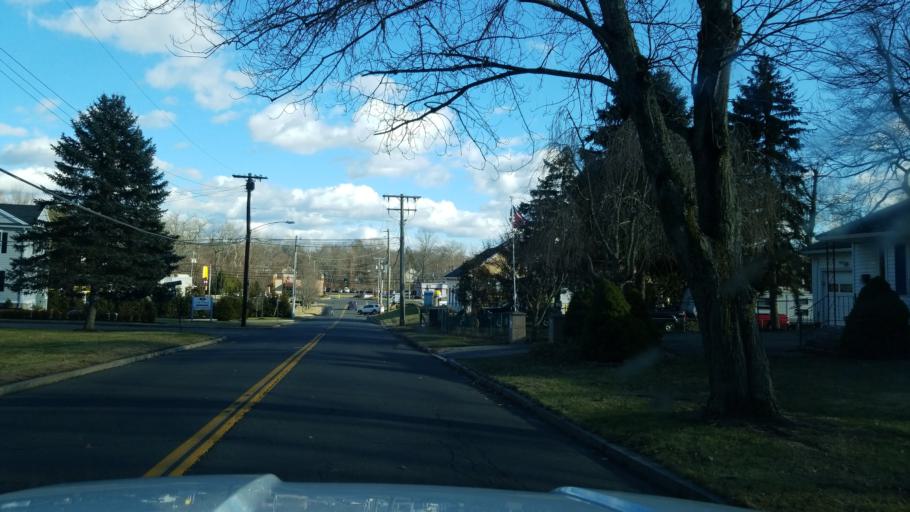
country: US
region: Connecticut
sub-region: Middlesex County
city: Middletown
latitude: 41.5405
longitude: -72.6554
